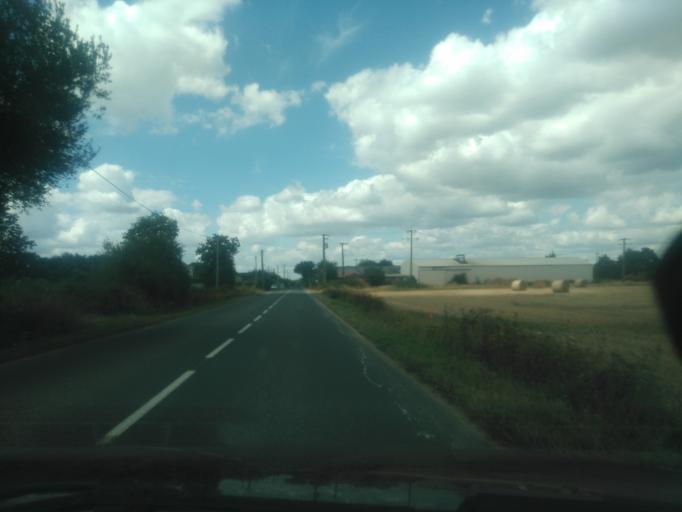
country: FR
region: Pays de la Loire
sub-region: Departement de la Vendee
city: Chauche
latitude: 46.8428
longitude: -1.2903
